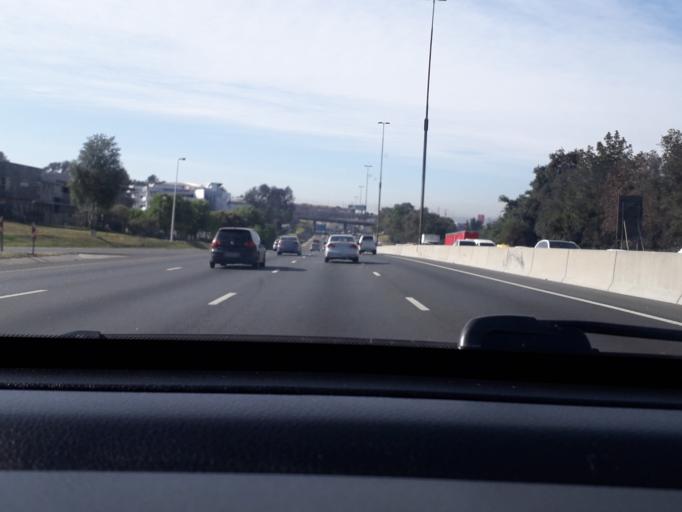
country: ZA
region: Gauteng
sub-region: City of Johannesburg Metropolitan Municipality
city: Modderfontein
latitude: -26.1172
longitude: 28.1335
